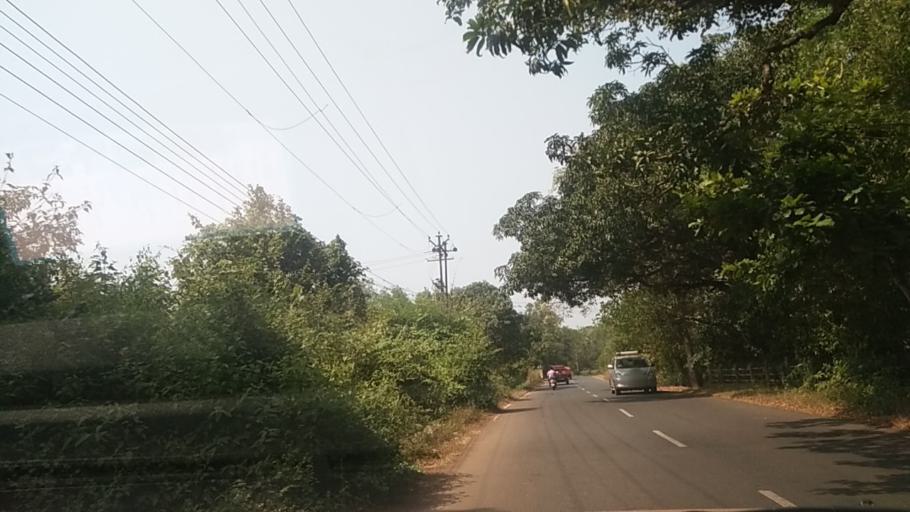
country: IN
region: Goa
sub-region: North Goa
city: Morjim
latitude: 15.6577
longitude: 73.7459
